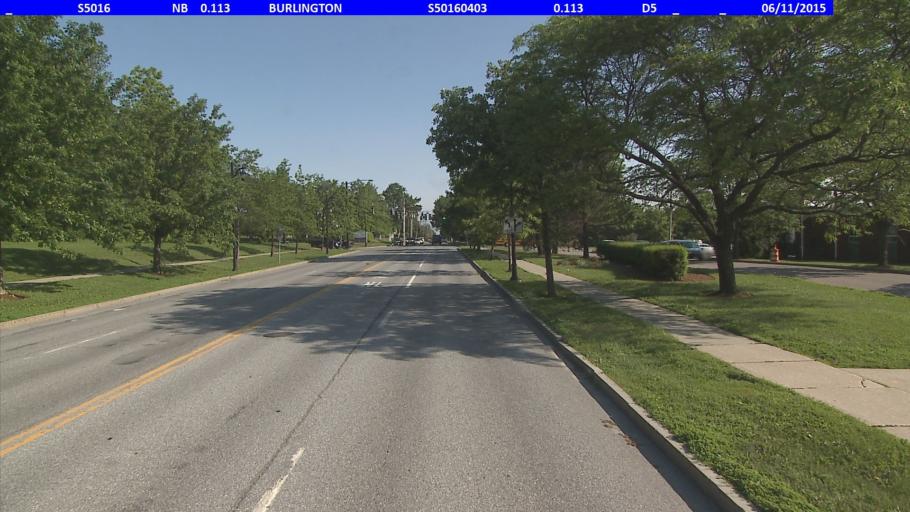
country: US
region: Vermont
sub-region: Chittenden County
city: Winooski
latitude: 44.4742
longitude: -73.1905
